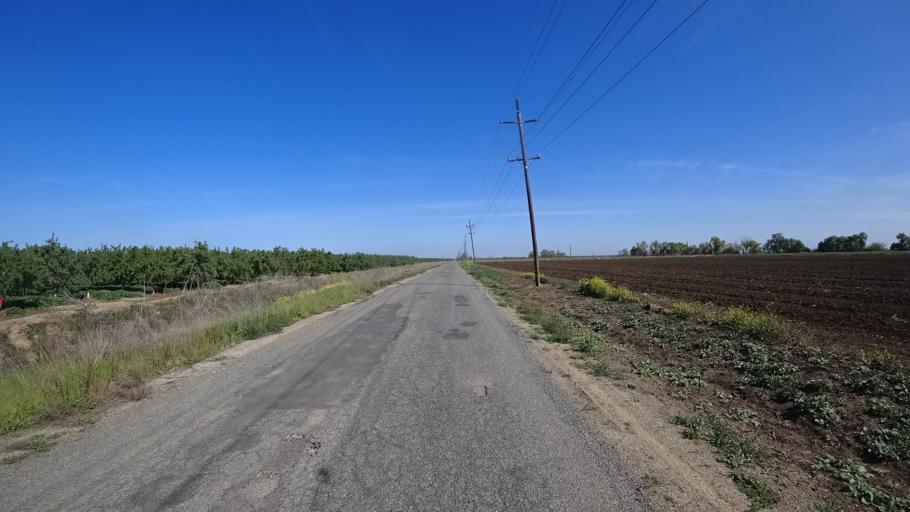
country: US
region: California
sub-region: Glenn County
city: Willows
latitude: 39.5406
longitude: -122.1860
